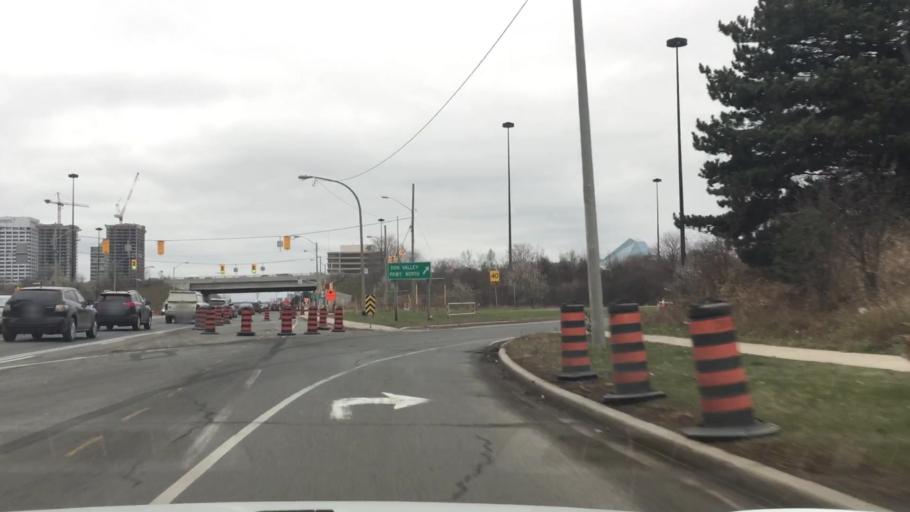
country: CA
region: Ontario
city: Willowdale
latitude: 43.7241
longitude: -79.3275
